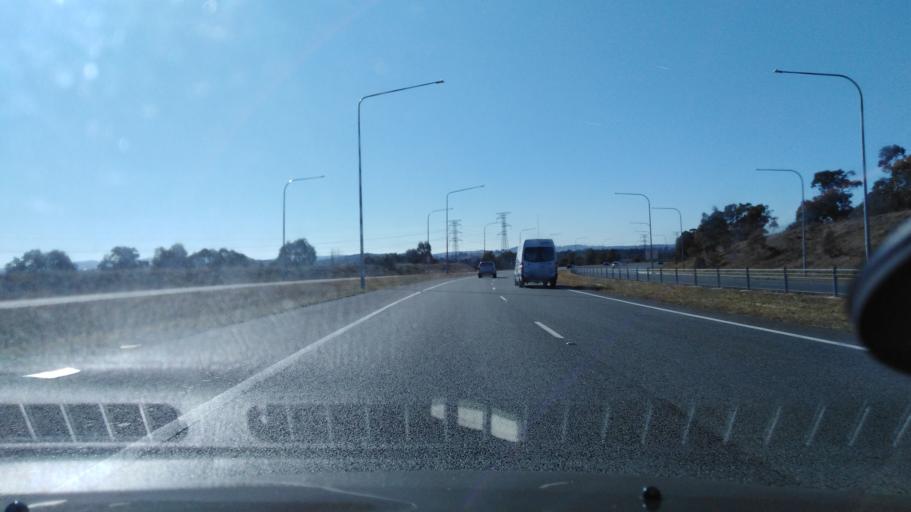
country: AU
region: Australian Capital Territory
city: Kaleen
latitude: -35.2416
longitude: 149.1109
